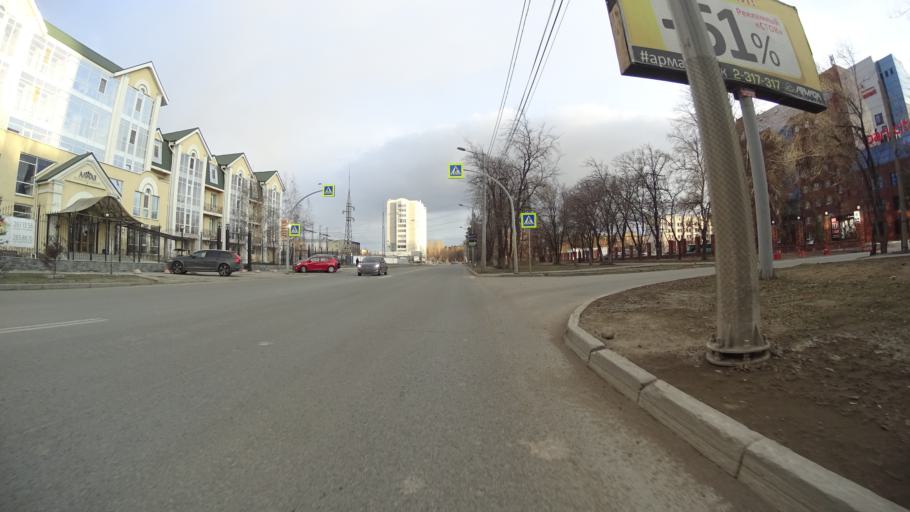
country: RU
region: Chelyabinsk
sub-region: Gorod Chelyabinsk
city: Chelyabinsk
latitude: 55.1506
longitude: 61.3651
